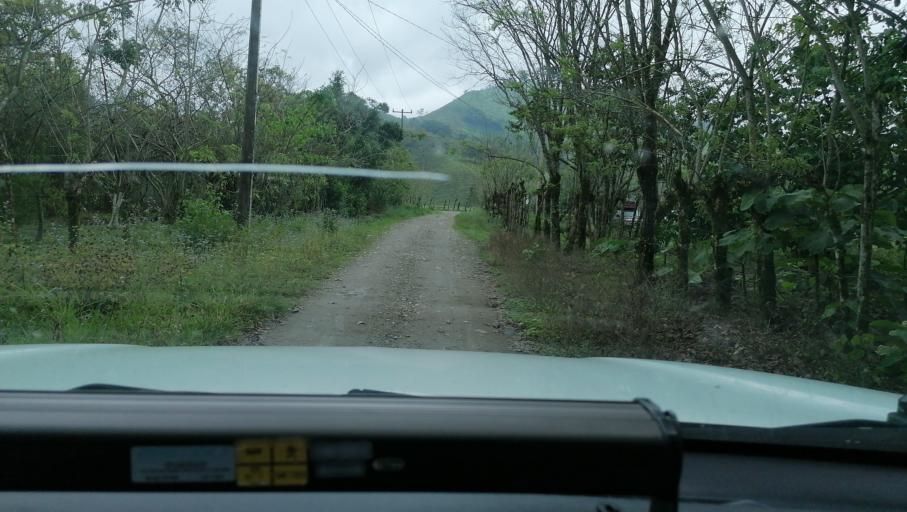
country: MX
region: Chiapas
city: Ixtacomitan
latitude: 17.3675
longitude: -93.1832
